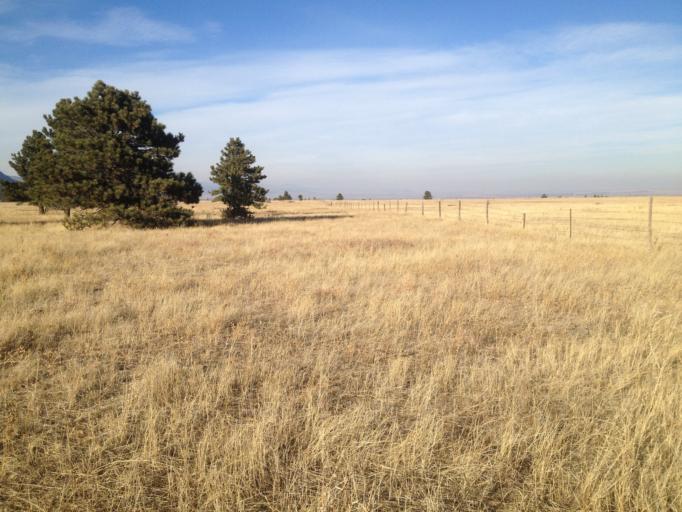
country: US
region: Colorado
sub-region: Boulder County
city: Superior
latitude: 39.9232
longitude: -105.2507
